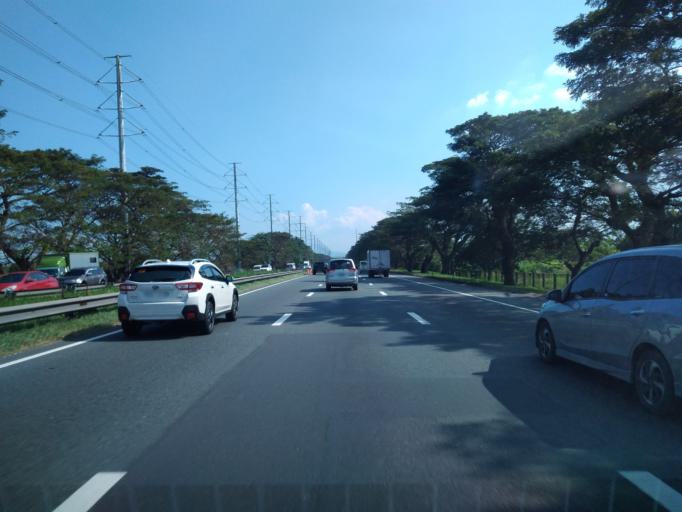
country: PH
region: Calabarzon
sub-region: Province of Laguna
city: Pulong Santa Cruz
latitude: 14.2644
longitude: 121.0989
